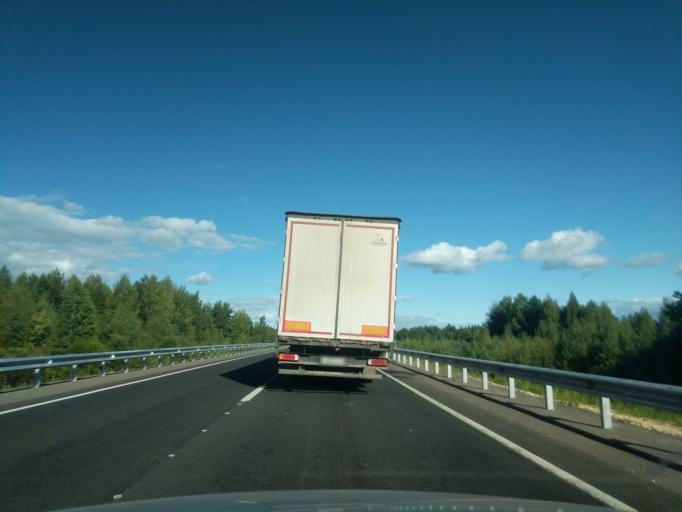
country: RU
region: Kostroma
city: Makar'yev
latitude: 57.8483
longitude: 43.6779
